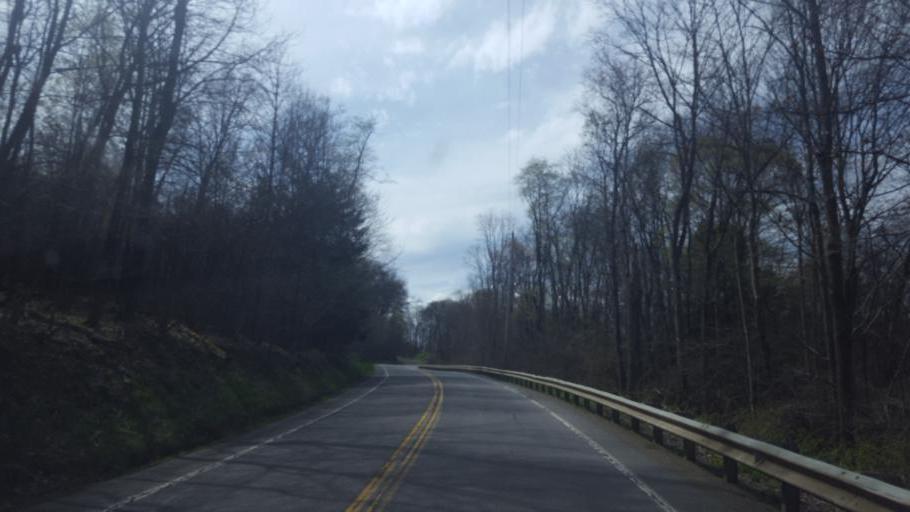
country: US
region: Pennsylvania
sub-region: Venango County
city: Sugarcreek
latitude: 41.3539
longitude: -79.9798
